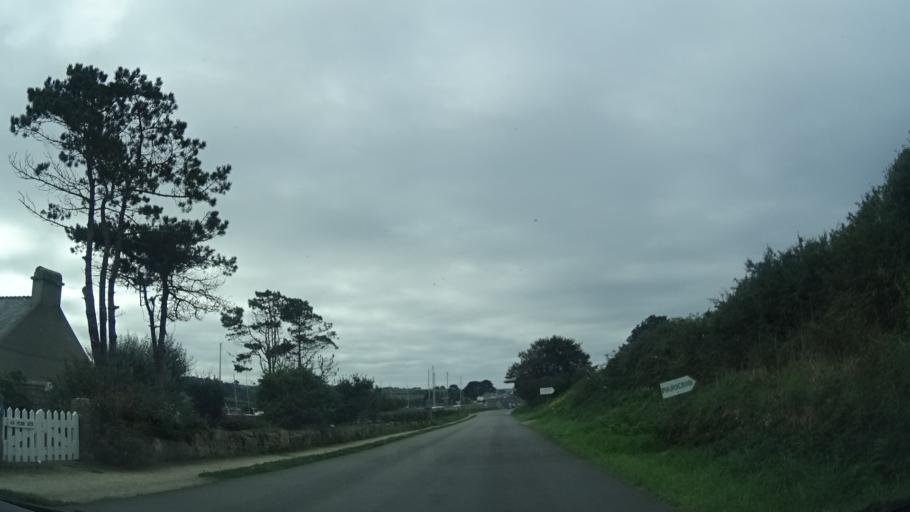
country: FR
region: Brittany
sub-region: Departement du Finistere
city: Lampaul-Plouarzel
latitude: 48.4727
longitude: -4.7568
